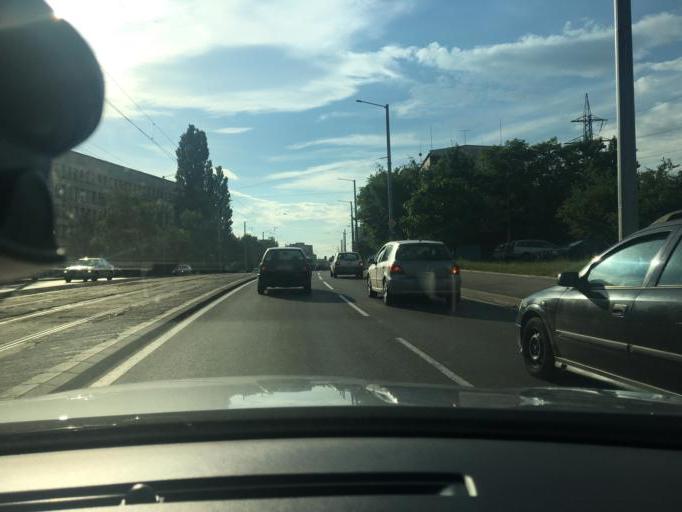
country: BG
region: Sofia-Capital
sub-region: Stolichna Obshtina
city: Sofia
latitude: 42.6759
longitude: 23.3721
